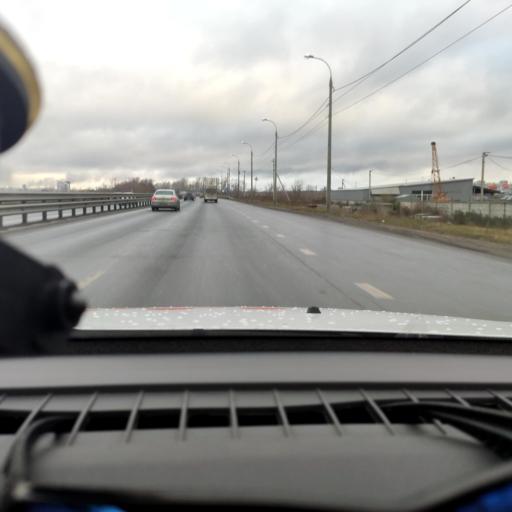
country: RU
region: Samara
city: Samara
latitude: 53.0968
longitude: 50.1539
